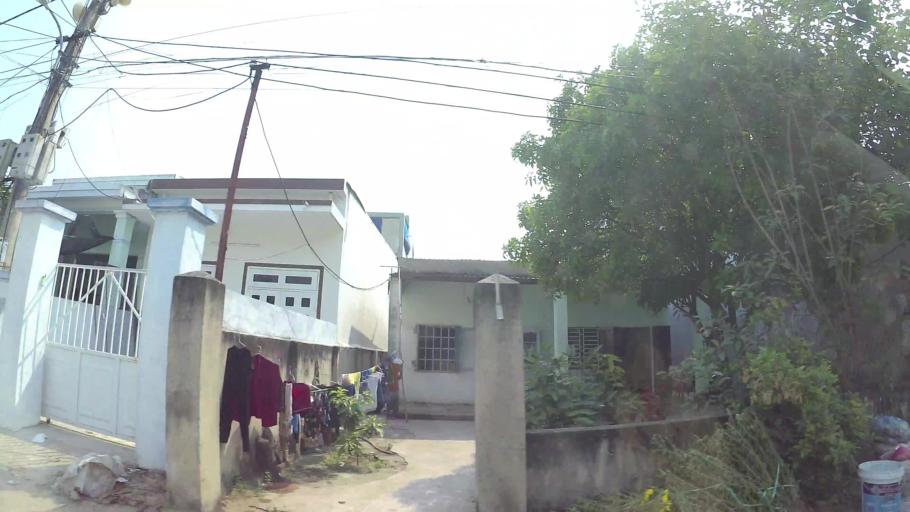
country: VN
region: Da Nang
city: Ngu Hanh Son
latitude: 15.9976
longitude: 108.2387
